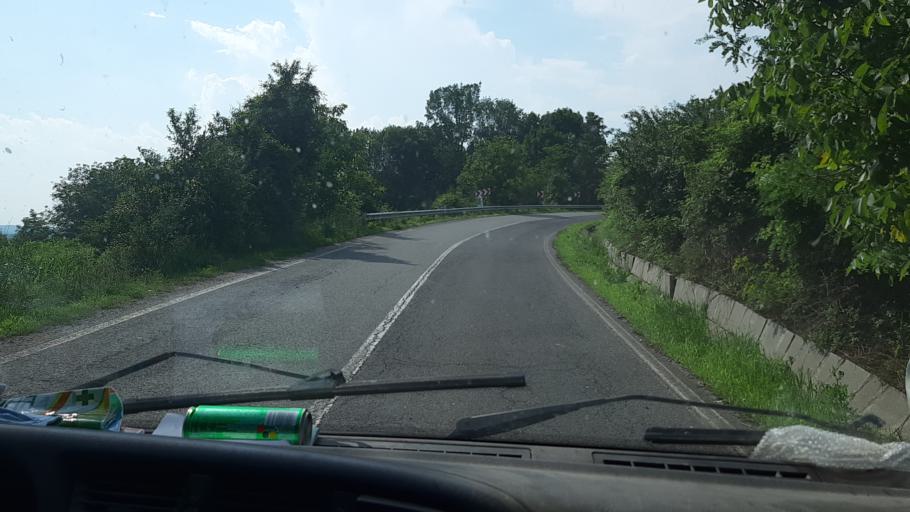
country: RO
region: Caras-Severin
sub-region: Comuna Farliug
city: Farliug
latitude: 45.5128
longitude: 21.8754
